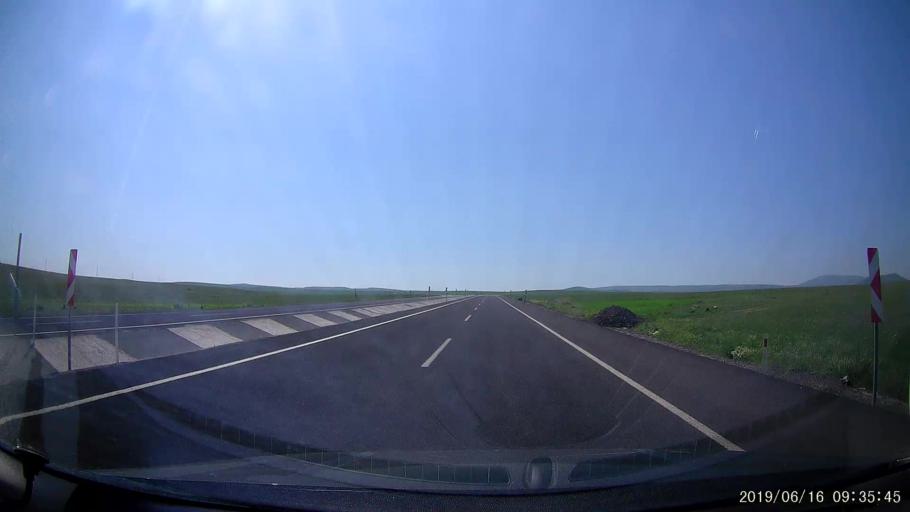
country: TR
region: Kars
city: Kars
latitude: 40.5669
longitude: 43.1611
